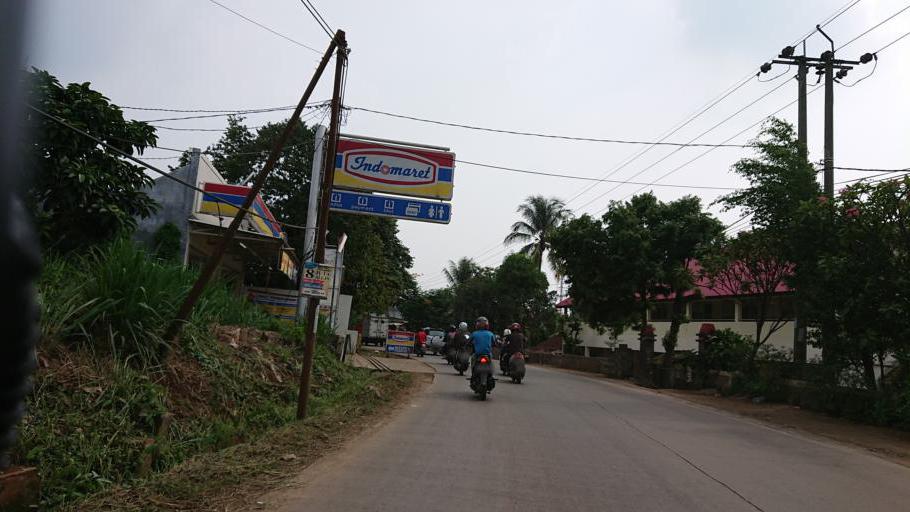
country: ID
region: West Java
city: Parung
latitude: -6.3816
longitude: 106.6803
